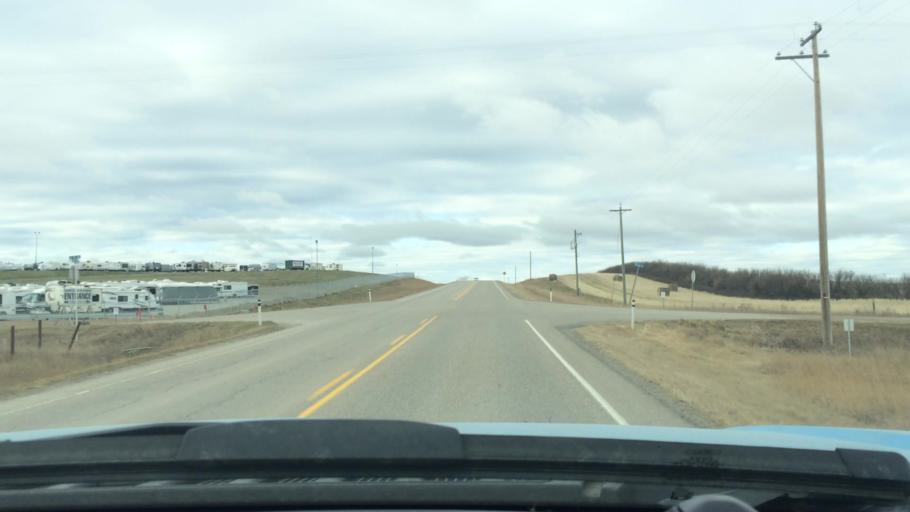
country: CA
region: Alberta
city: Airdrie
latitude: 51.2126
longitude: -114.0475
